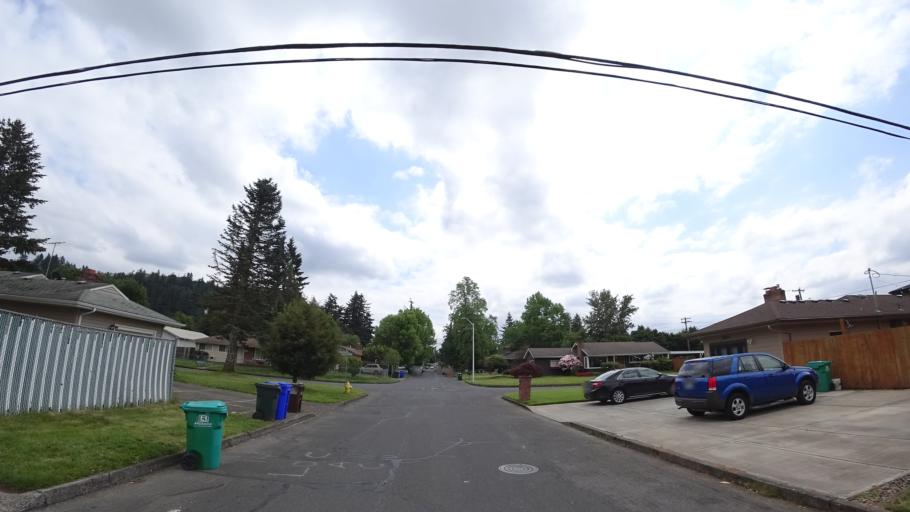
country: US
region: Oregon
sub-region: Multnomah County
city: Gresham
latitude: 45.5058
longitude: -122.4724
